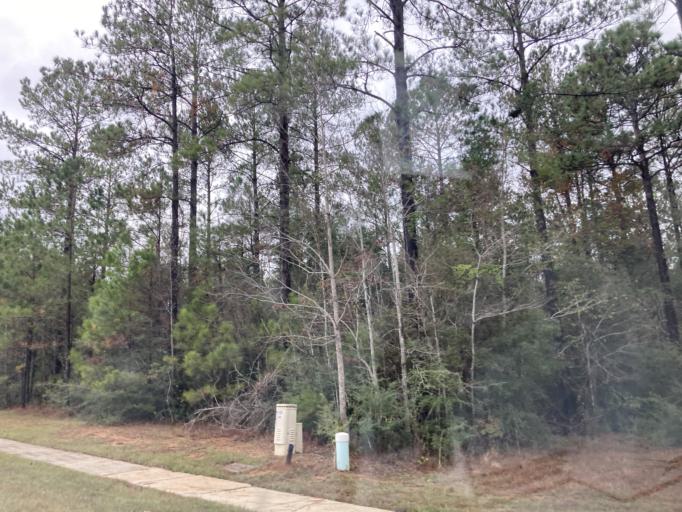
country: US
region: Mississippi
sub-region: Lamar County
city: West Hattiesburg
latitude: 31.2844
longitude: -89.4796
